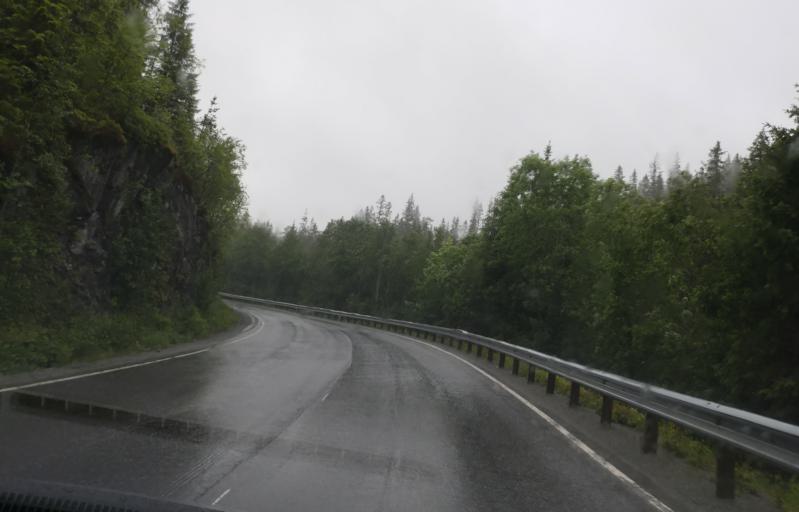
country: NO
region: Sor-Trondelag
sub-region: Selbu
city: Mebonden
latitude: 63.3547
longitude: 11.0751
